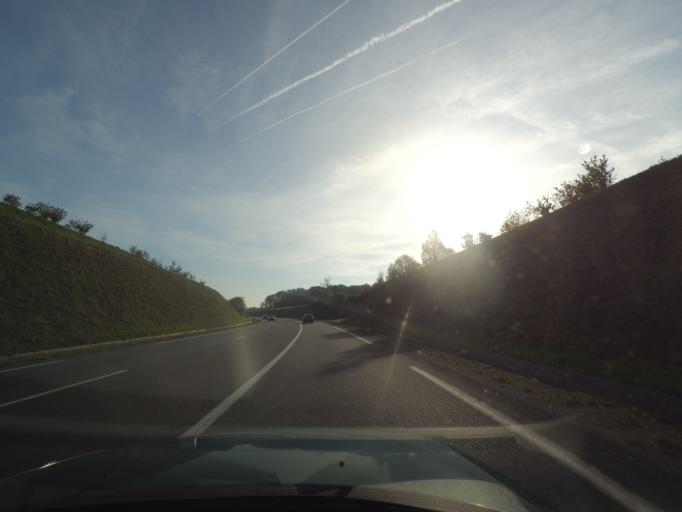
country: FR
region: Pays de la Loire
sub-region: Departement de la Vendee
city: Bouffere
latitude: 46.9604
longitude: -1.3200
